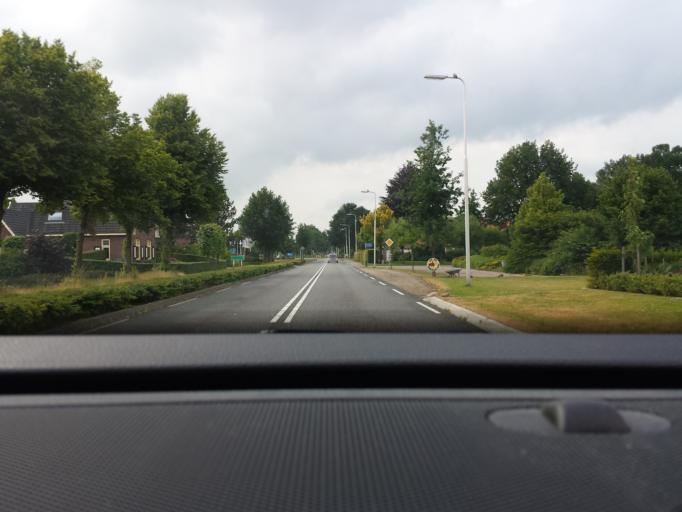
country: NL
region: Gelderland
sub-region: Gemeente Lochem
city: Barchem
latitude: 52.0799
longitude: 6.4610
